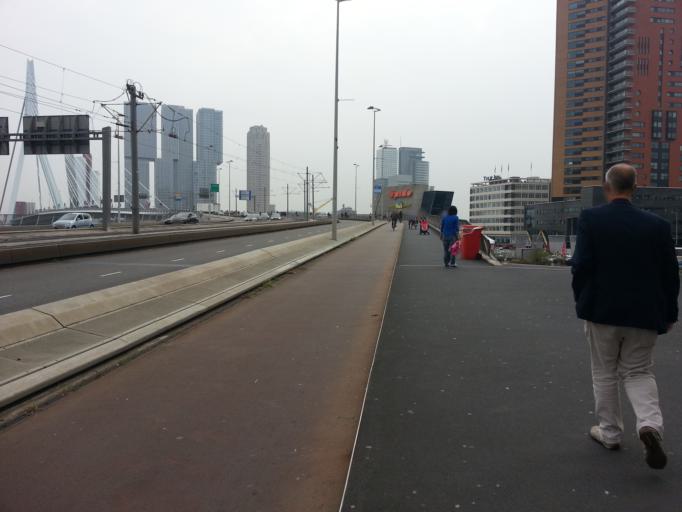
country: NL
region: South Holland
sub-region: Gemeente Rotterdam
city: Rotterdam
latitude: 51.9117
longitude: 4.4821
